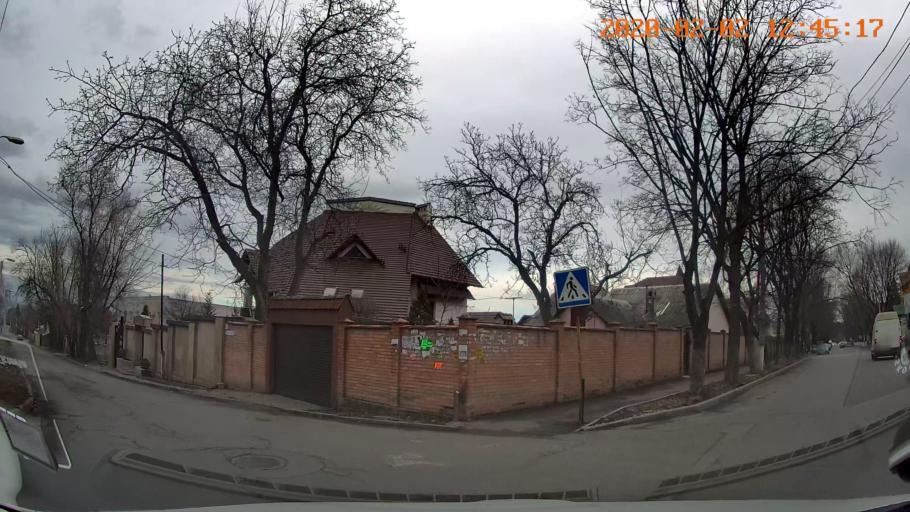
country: MD
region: Chisinau
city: Chisinau
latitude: 47.0048
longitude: 28.8126
